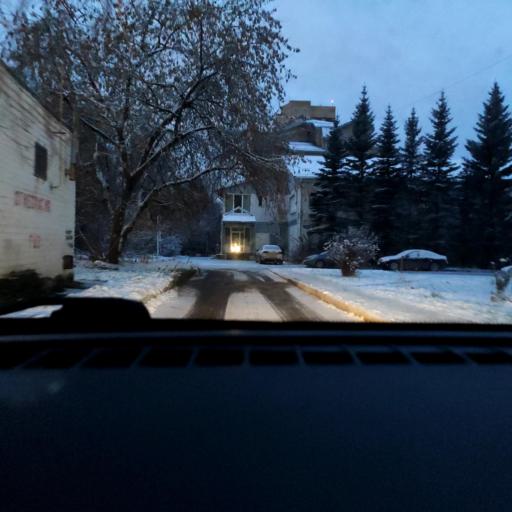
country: RU
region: Perm
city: Perm
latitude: 57.9815
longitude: 56.1893
